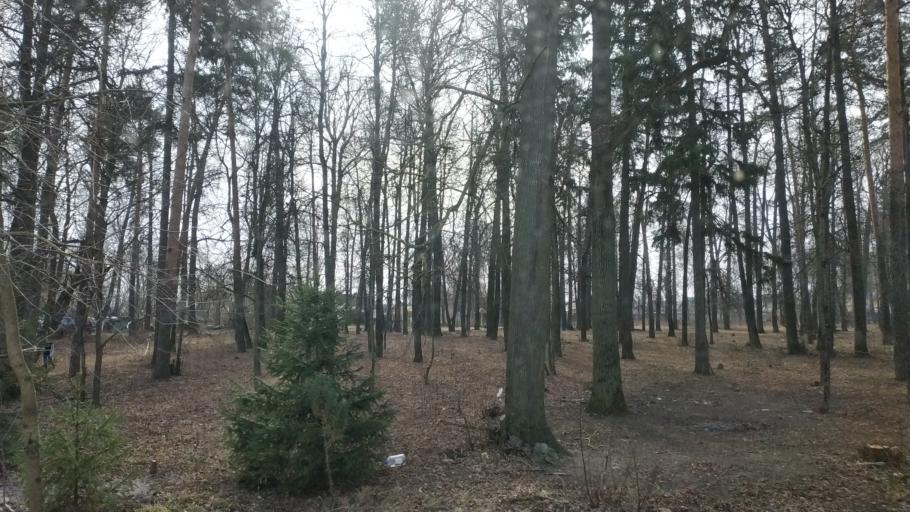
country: RU
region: Moskovskaya
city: Peski
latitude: 55.2589
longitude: 38.7227
